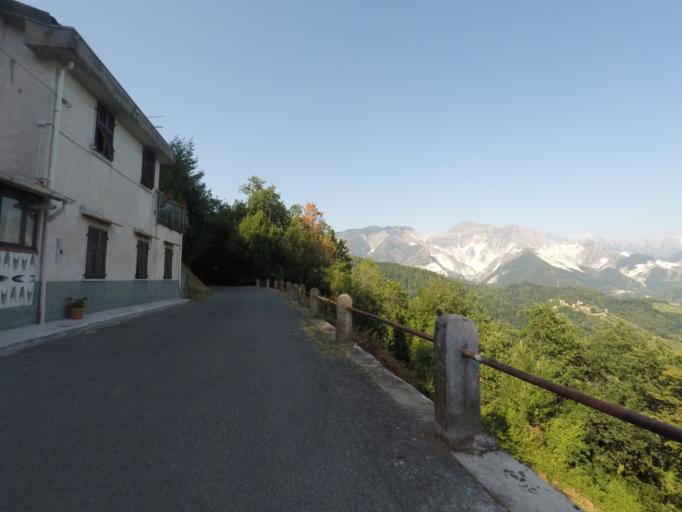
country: IT
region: Tuscany
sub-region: Provincia di Massa-Carrara
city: Carrara
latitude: 44.0768
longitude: 10.0660
